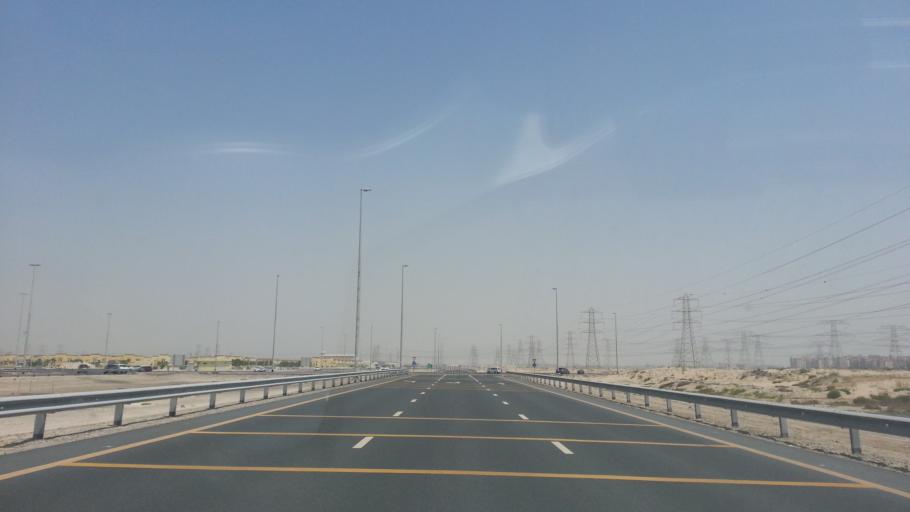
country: AE
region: Dubai
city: Dubai
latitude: 25.0415
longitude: 55.1547
